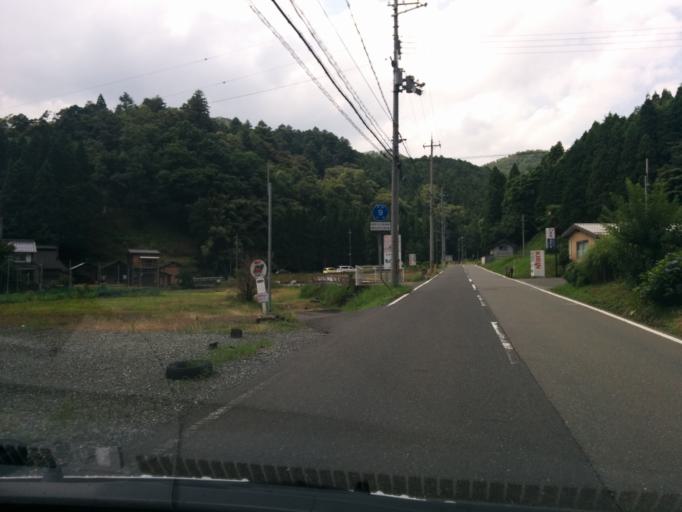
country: JP
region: Kyoto
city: Miyazu
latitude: 35.4260
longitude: 135.1575
